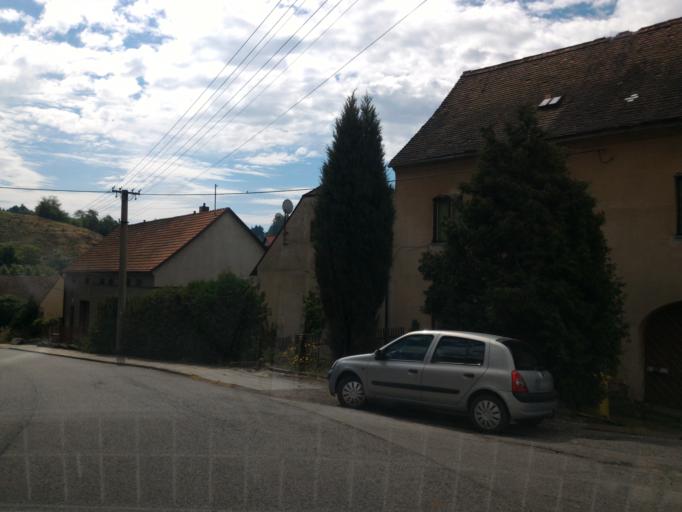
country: CZ
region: Vysocina
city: Zeletava
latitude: 49.1387
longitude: 15.5640
